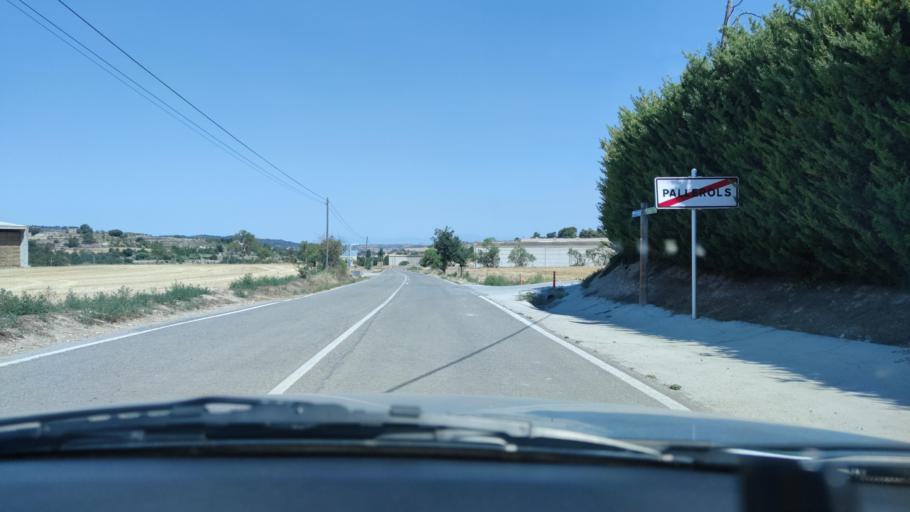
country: ES
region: Catalonia
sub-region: Provincia de Lleida
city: Sant Guim de Freixenet
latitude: 41.6194
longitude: 1.3527
